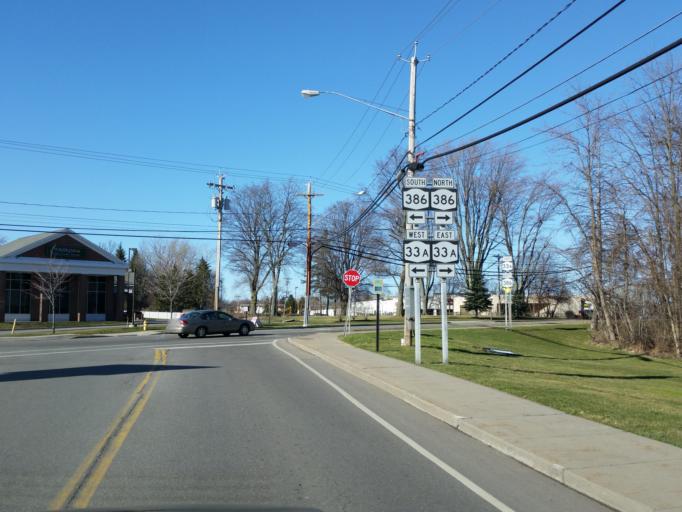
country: US
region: New York
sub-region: Monroe County
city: Scottsville
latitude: 43.1030
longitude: -77.7537
